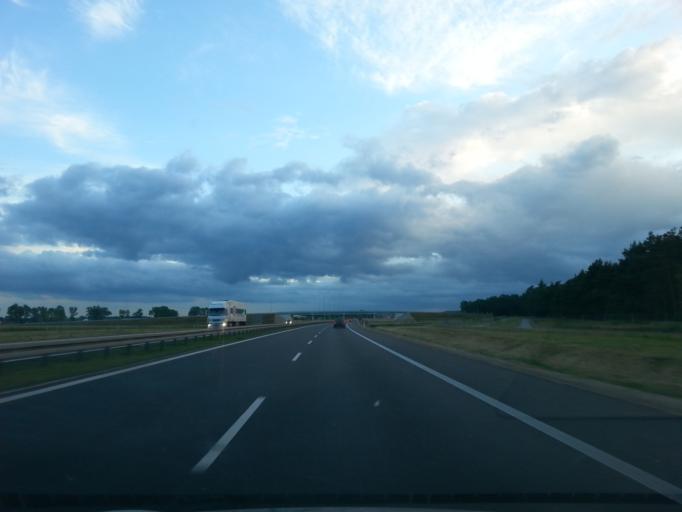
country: PL
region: Lower Silesian Voivodeship
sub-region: Powiat olesnicki
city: Olesnica
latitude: 51.2336
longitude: 17.4834
